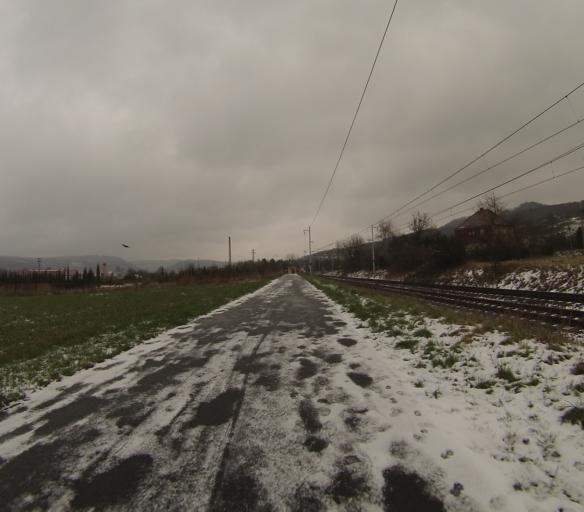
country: CZ
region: Ustecky
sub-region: Okres Decin
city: Decin
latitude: 50.7537
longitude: 14.1989
